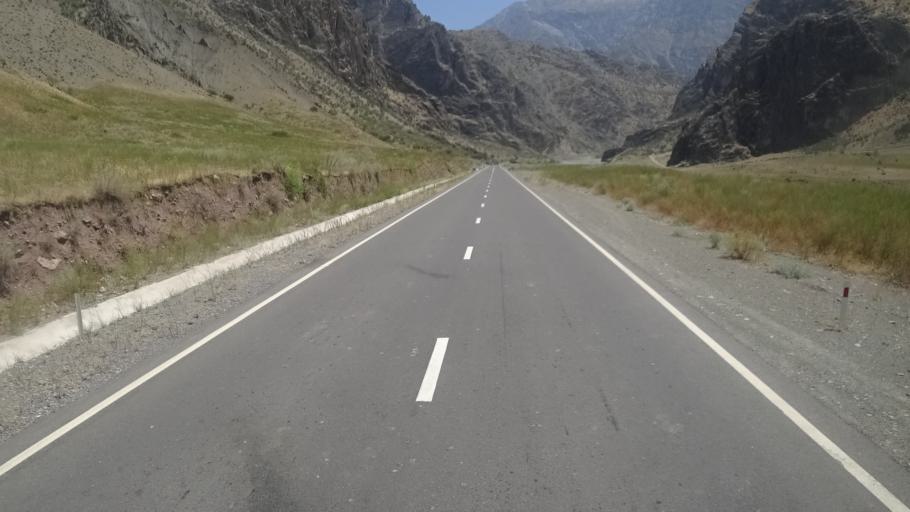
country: AF
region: Badakhshan
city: Deh Khwahan
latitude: 37.9424
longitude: 70.2345
